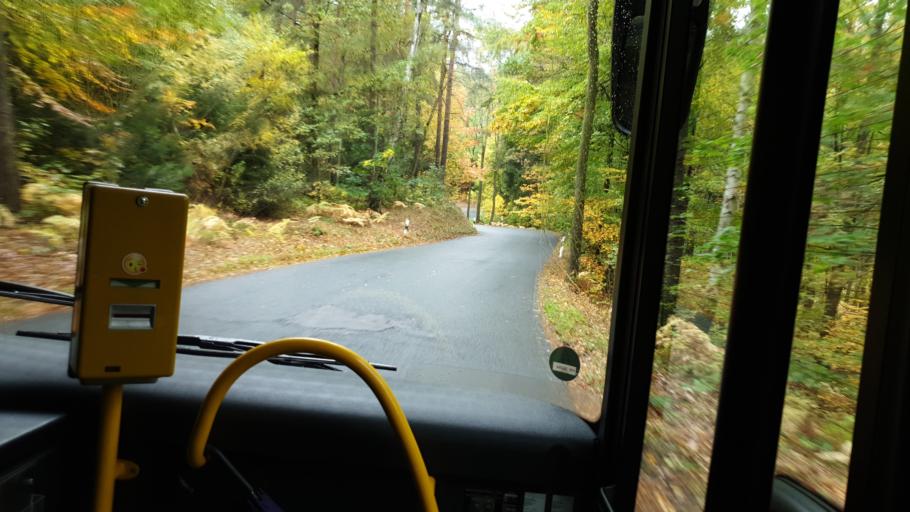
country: DE
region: Saxony
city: Kurort Gohrisch
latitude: 50.9048
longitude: 14.1124
